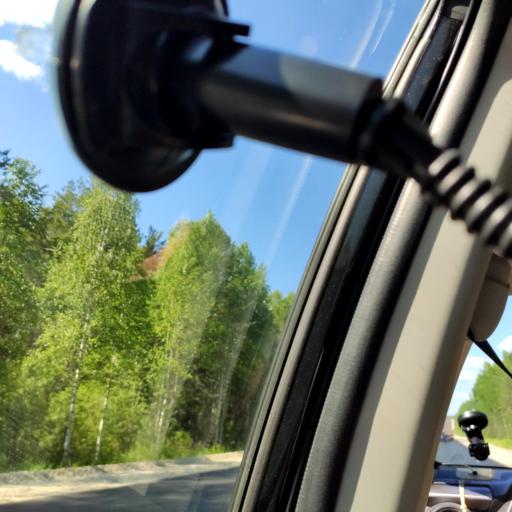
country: RU
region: Mariy-El
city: Suslonger
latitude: 56.2628
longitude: 48.2327
